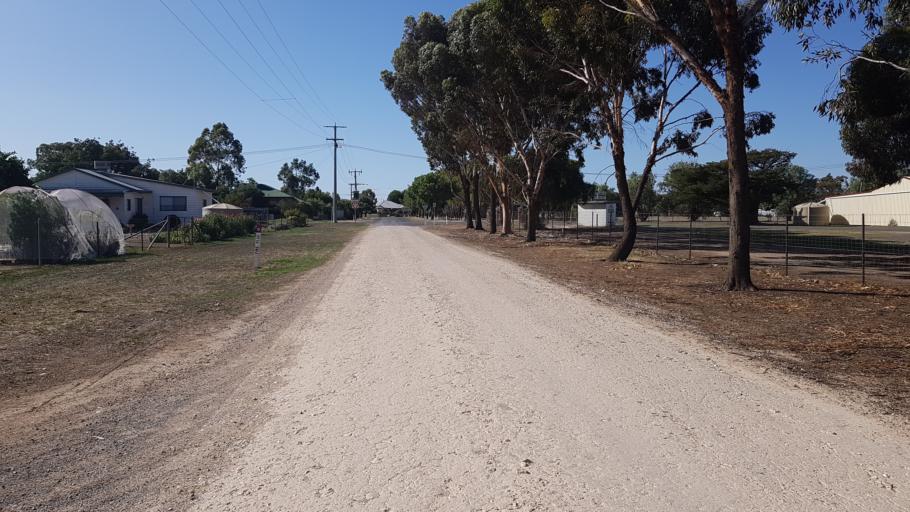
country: AU
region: Victoria
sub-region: Horsham
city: Horsham
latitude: -36.7427
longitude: 141.9473
